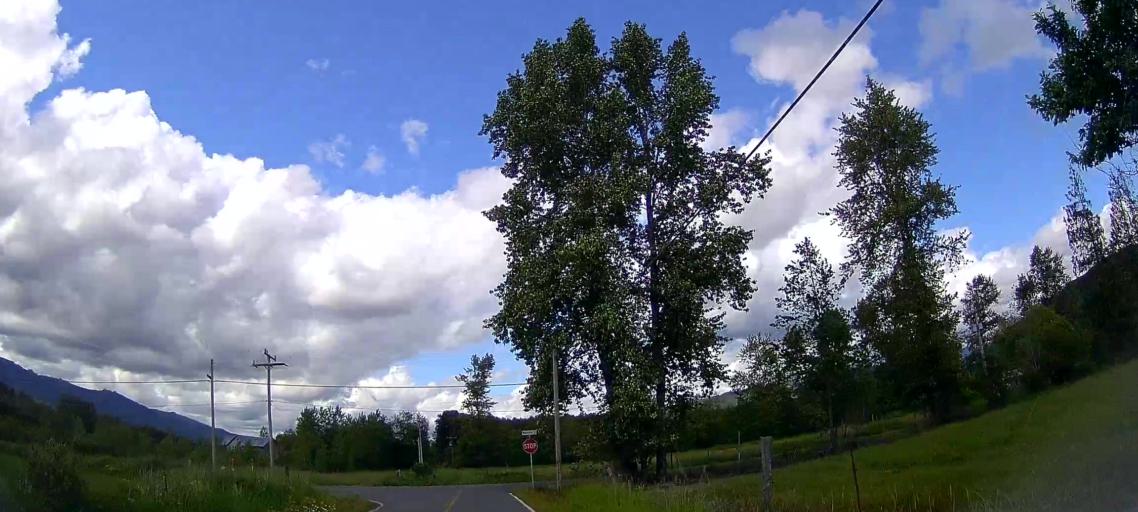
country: US
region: Washington
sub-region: Whatcom County
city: Sudden Valley
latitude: 48.6922
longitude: -122.1879
